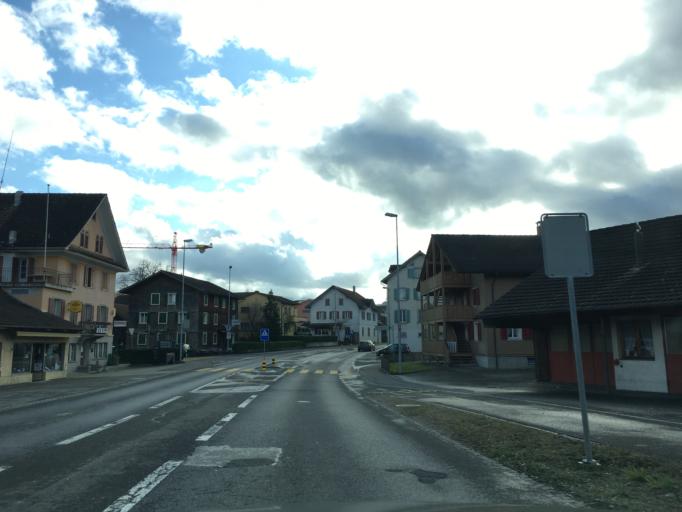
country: CH
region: Aargau
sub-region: Bezirk Muri
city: Oberruti
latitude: 47.1665
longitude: 8.3941
